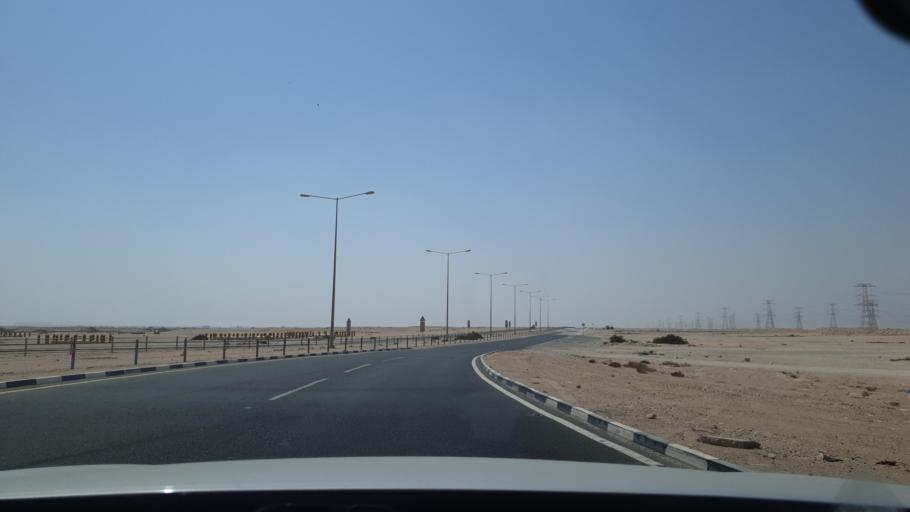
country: QA
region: Al Khawr
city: Al Khawr
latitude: 25.7313
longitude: 51.4576
